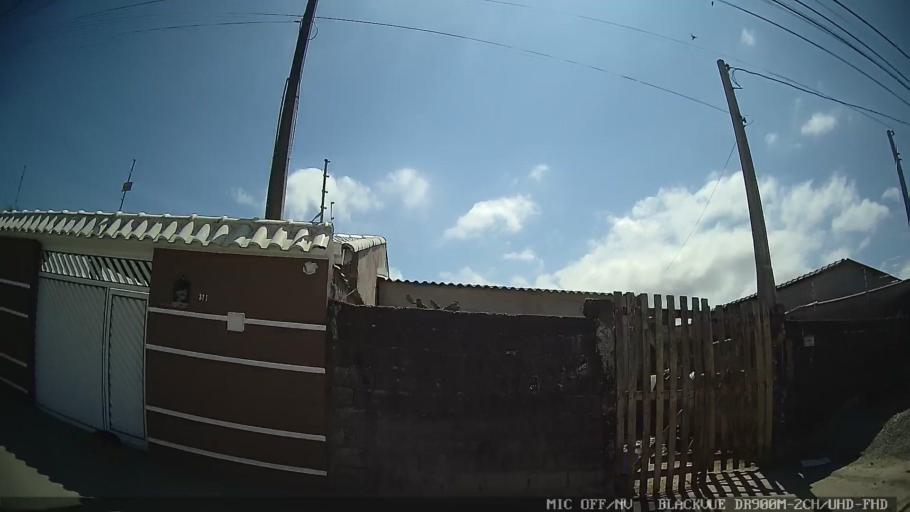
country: BR
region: Sao Paulo
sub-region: Peruibe
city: Peruibe
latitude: -24.3007
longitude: -47.0006
